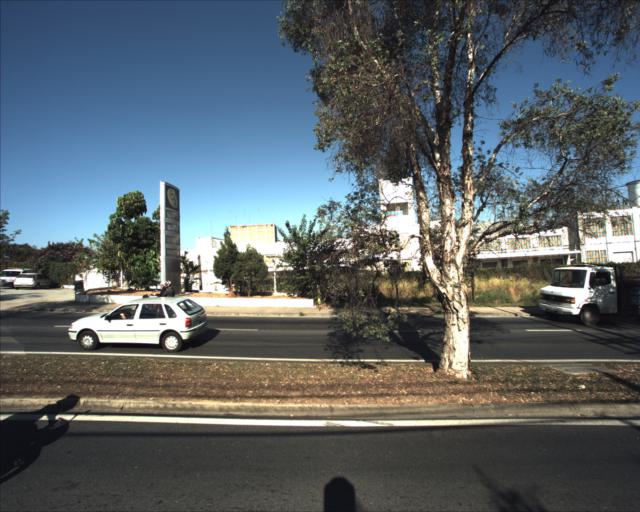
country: BR
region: Sao Paulo
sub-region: Sorocaba
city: Sorocaba
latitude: -23.4837
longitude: -47.4269
